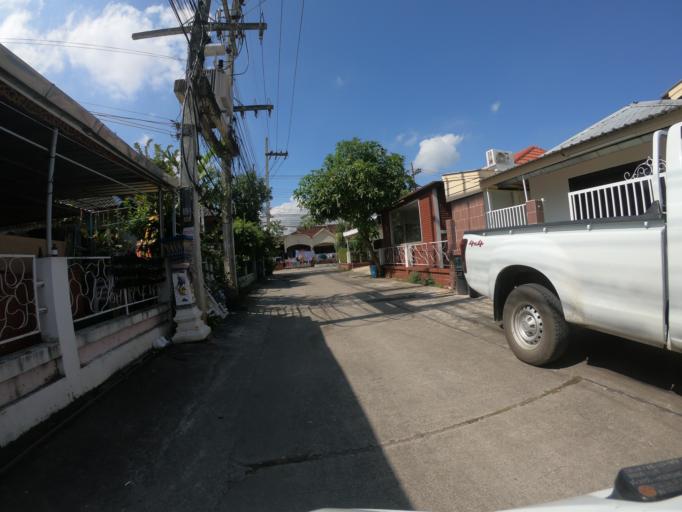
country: TH
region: Chiang Mai
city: Chiang Mai
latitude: 18.7409
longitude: 98.9523
